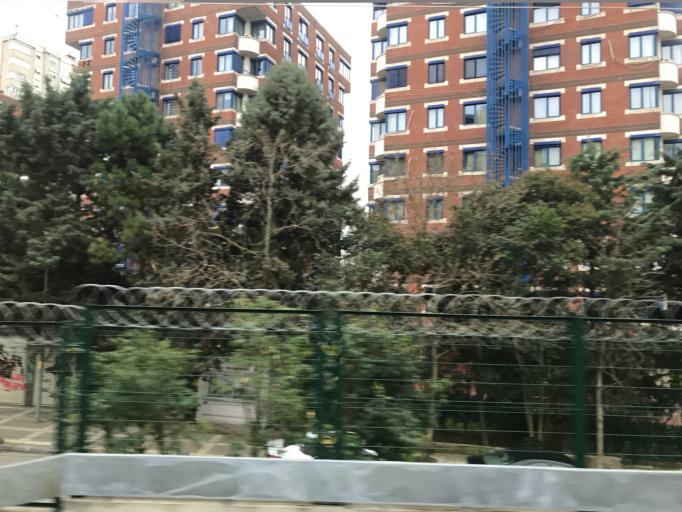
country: TR
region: Istanbul
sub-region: Atasehir
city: Atasehir
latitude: 40.9602
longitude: 29.0851
